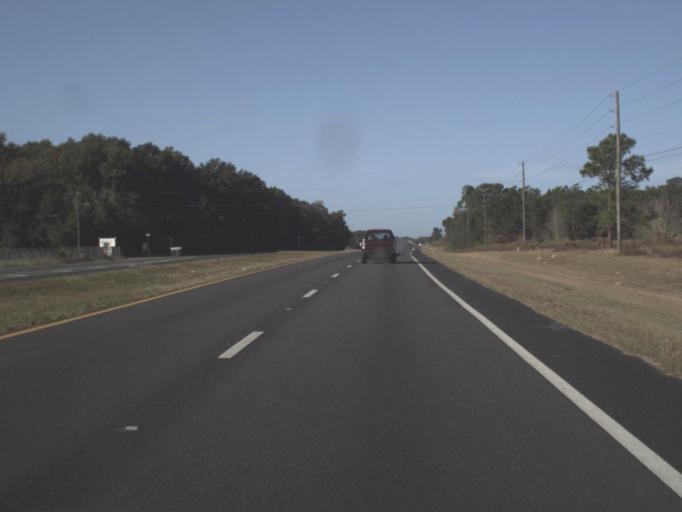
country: US
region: Florida
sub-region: Marion County
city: Belleview
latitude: 29.0259
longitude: -82.1246
